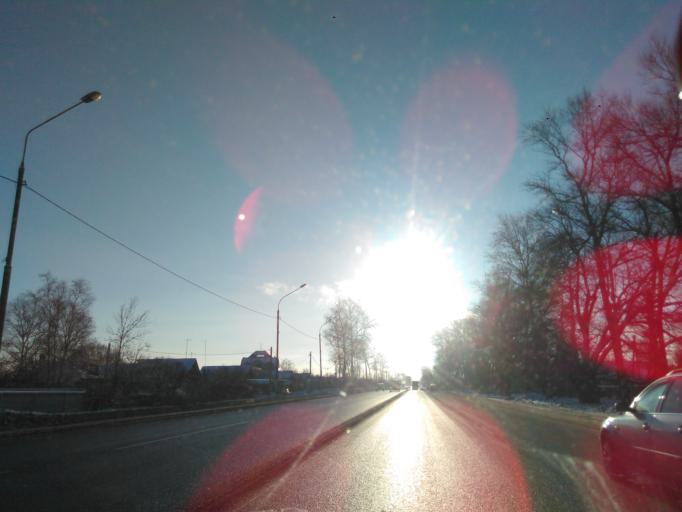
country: RU
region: Moskovskaya
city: Klin
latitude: 56.3579
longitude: 36.6964
